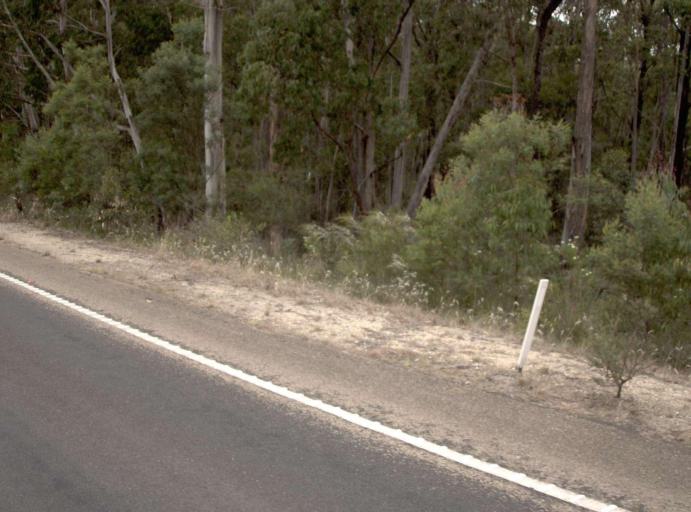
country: AU
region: Victoria
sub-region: East Gippsland
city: Lakes Entrance
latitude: -37.6899
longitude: 148.0332
